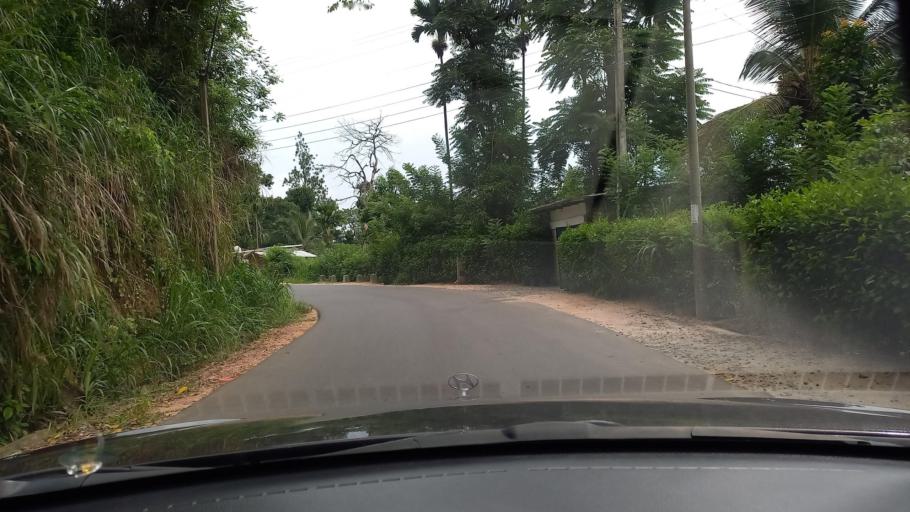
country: LK
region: Central
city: Gampola
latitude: 7.2076
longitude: 80.6258
